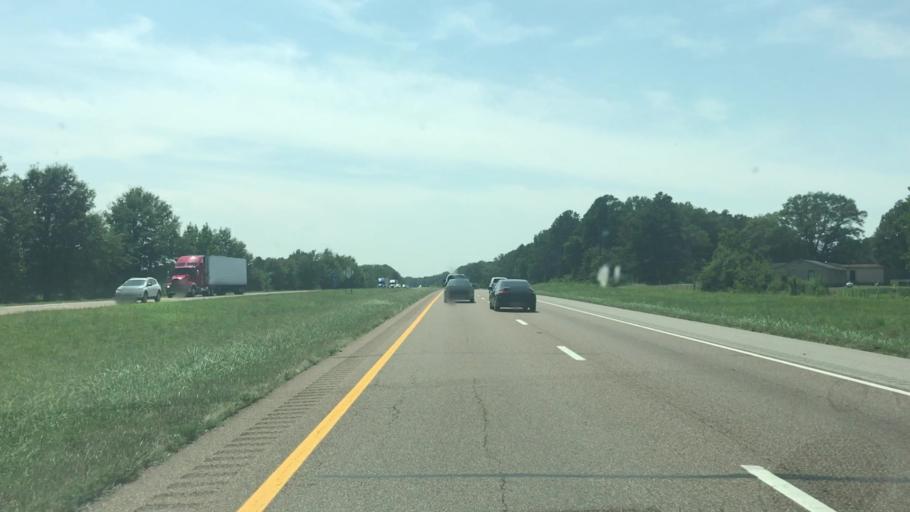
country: US
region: Tennessee
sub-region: Tipton County
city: Mason
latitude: 35.3377
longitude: -89.5430
